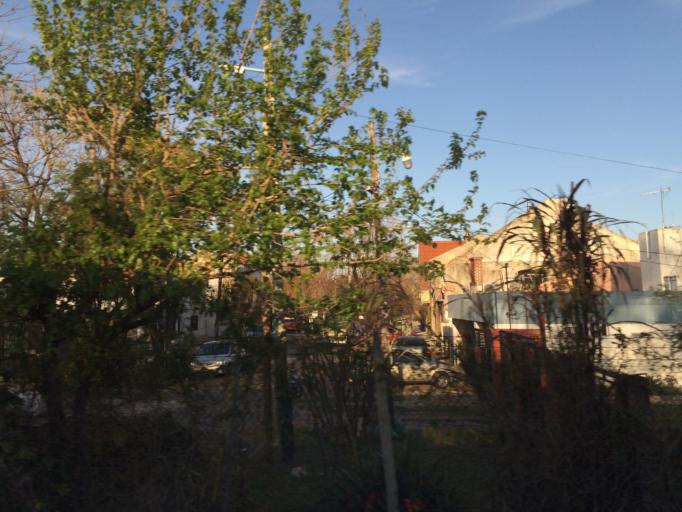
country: AR
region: Buenos Aires
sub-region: Partido de Lomas de Zamora
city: Lomas de Zamora
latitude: -34.7373
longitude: -58.3946
